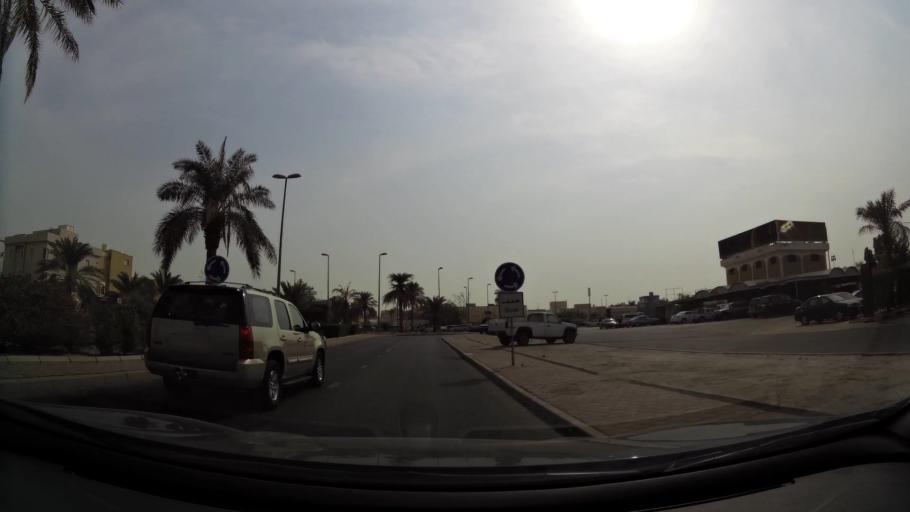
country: KW
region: Al Asimah
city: Ar Rabiyah
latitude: 29.2871
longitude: 47.9426
